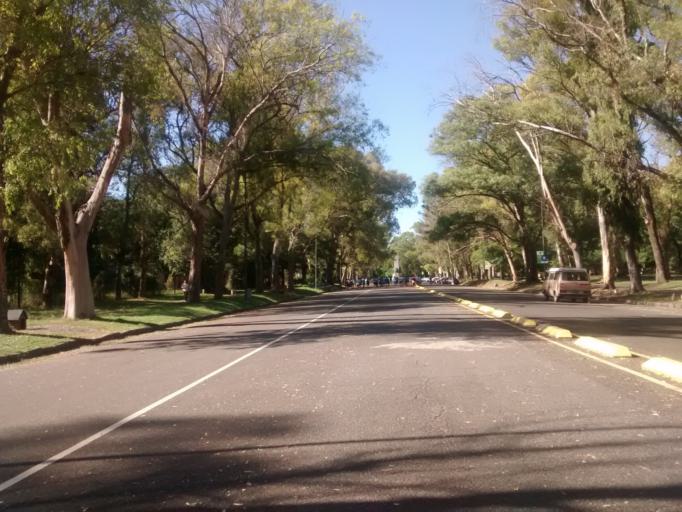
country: AR
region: Buenos Aires
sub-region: Partido de La Plata
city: La Plata
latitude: -34.9065
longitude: -57.9336
